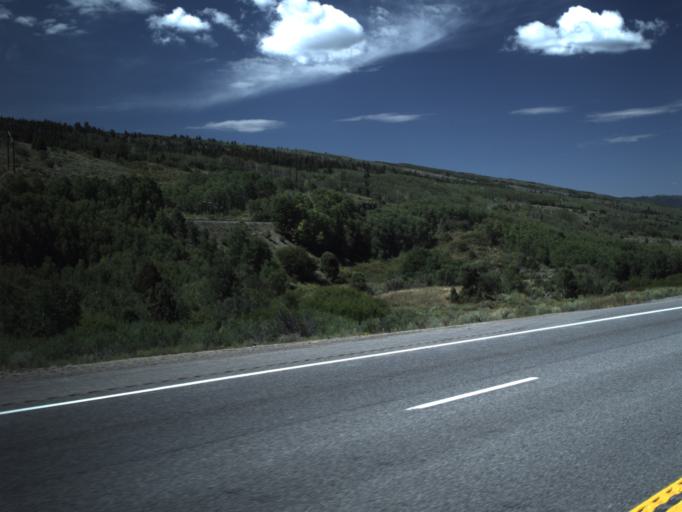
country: US
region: Utah
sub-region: Carbon County
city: Helper
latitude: 39.9339
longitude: -111.0995
